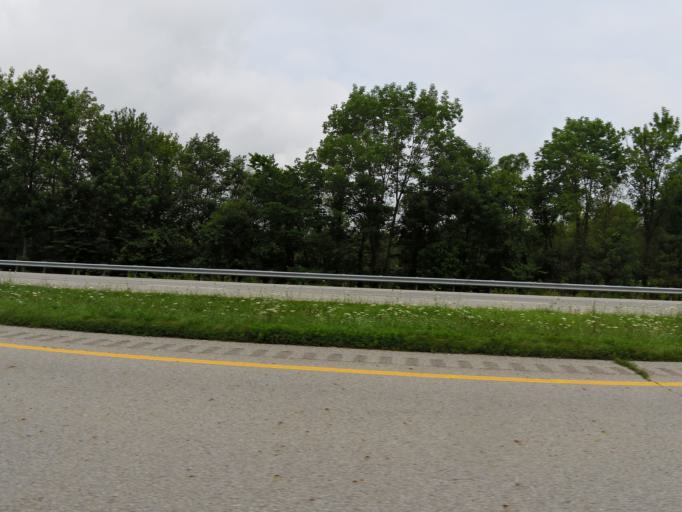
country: US
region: Kentucky
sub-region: Ohio County
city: Beaver Dam
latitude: 37.3505
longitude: -86.9239
